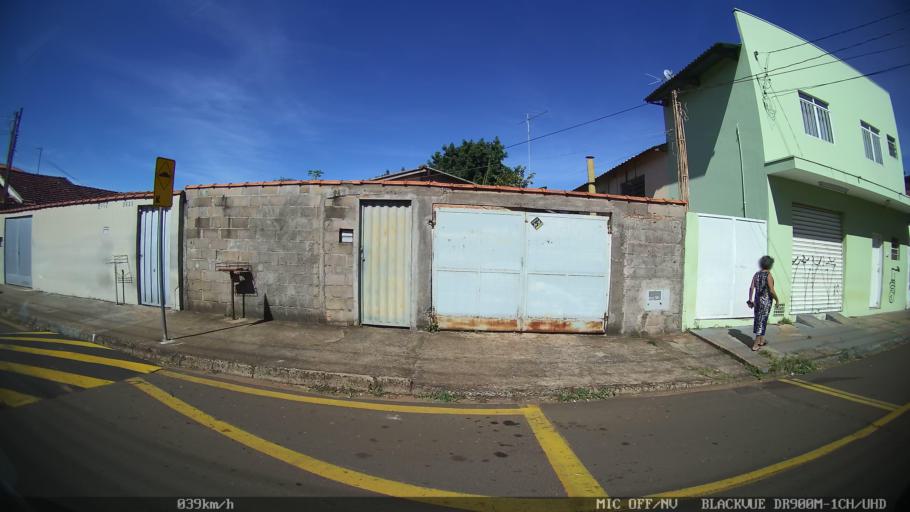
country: BR
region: Sao Paulo
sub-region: Franca
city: Franca
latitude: -20.5470
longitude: -47.3840
